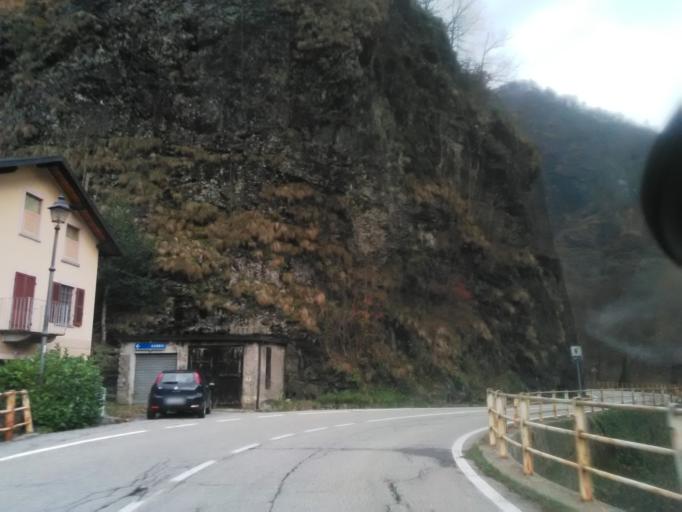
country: IT
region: Piedmont
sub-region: Provincia di Vercelli
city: Sabbia
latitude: 45.8533
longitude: 8.2391
